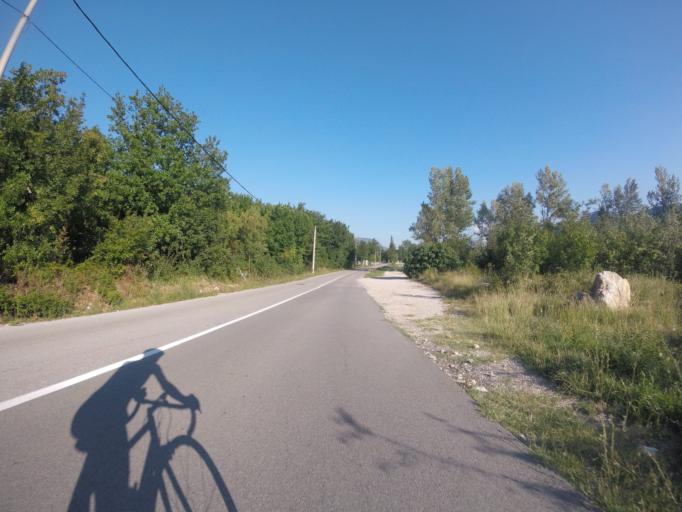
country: HR
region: Primorsko-Goranska
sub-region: Grad Crikvenica
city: Jadranovo
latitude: 45.2288
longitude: 14.6691
